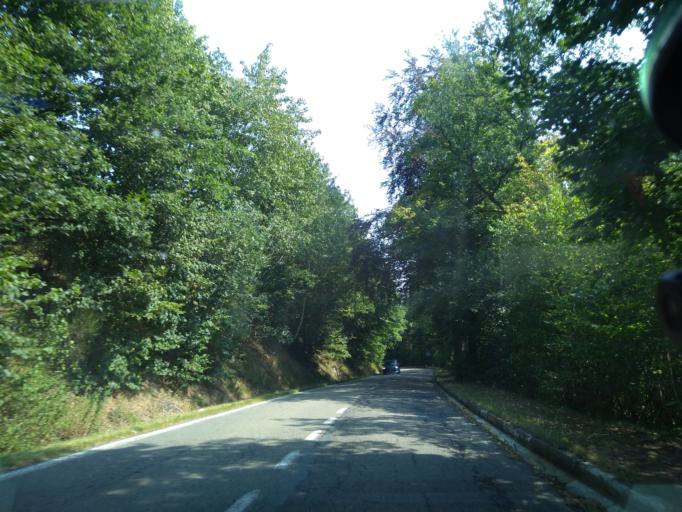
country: BE
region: Wallonia
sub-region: Province du Luxembourg
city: La Roche-en-Ardenne
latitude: 50.1693
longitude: 5.5657
